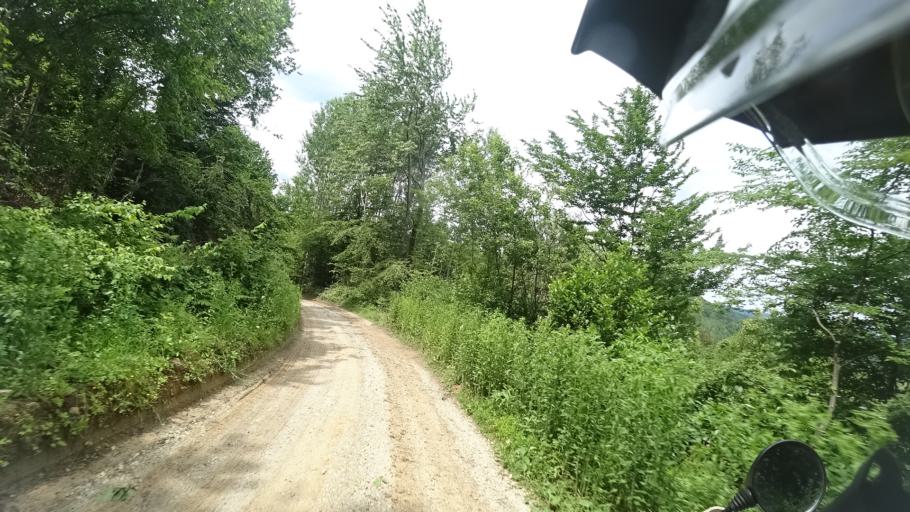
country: HR
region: Karlovacka
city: Vojnic
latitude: 45.2459
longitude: 15.7037
